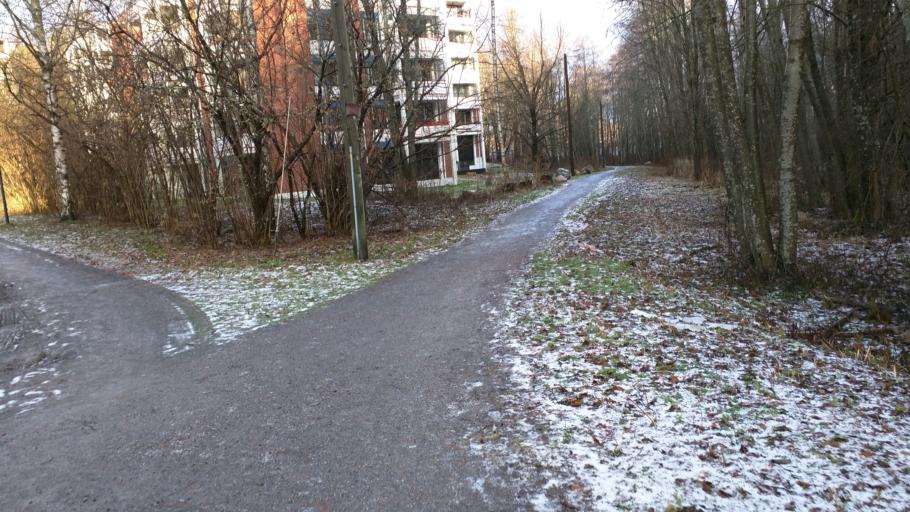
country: FI
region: Uusimaa
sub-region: Helsinki
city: Kilo
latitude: 60.2610
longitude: 24.8087
